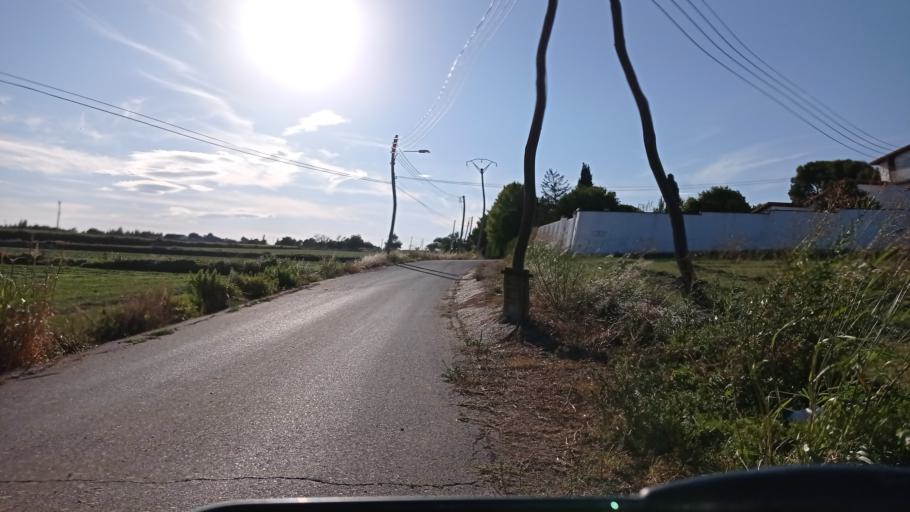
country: ES
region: Aragon
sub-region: Provincia de Zaragoza
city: Oliver-Valdefierro, Oliver, Valdefierro
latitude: 41.6655
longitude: -0.9603
